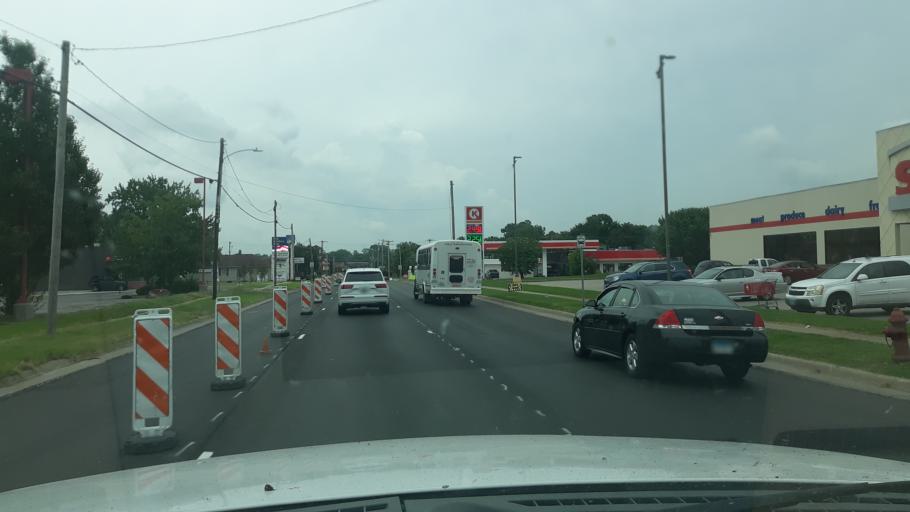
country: US
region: Illinois
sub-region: Jackson County
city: Carbondale
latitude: 37.7255
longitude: -89.2135
